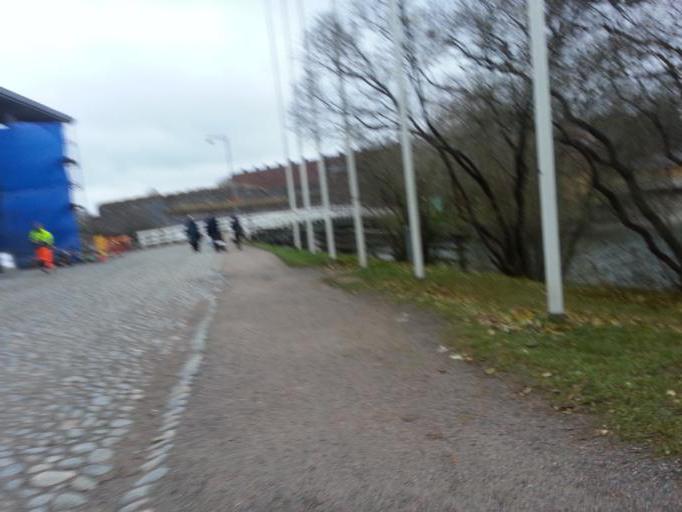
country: FI
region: Uusimaa
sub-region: Helsinki
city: Helsinki
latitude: 60.1455
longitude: 24.9875
